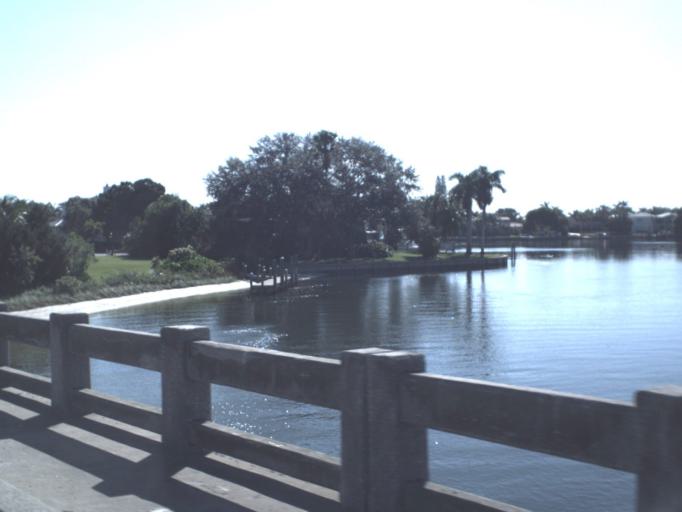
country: US
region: Florida
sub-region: Sarasota County
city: Siesta Key
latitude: 27.3248
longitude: -82.5652
